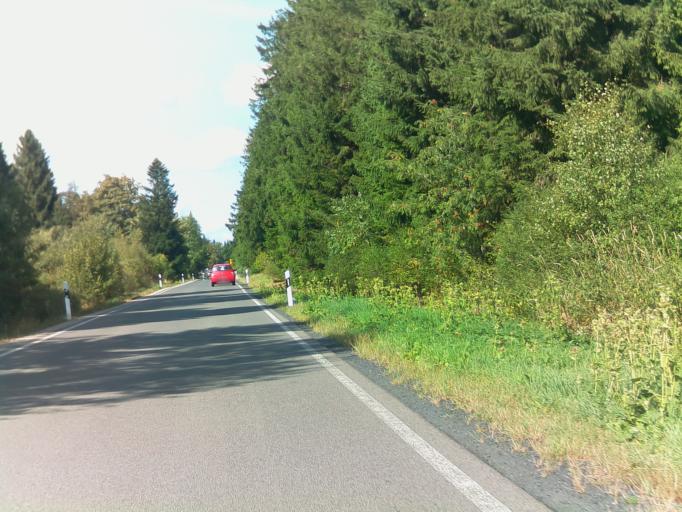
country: DE
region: Thuringia
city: Frankenheim
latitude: 50.5189
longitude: 10.0729
